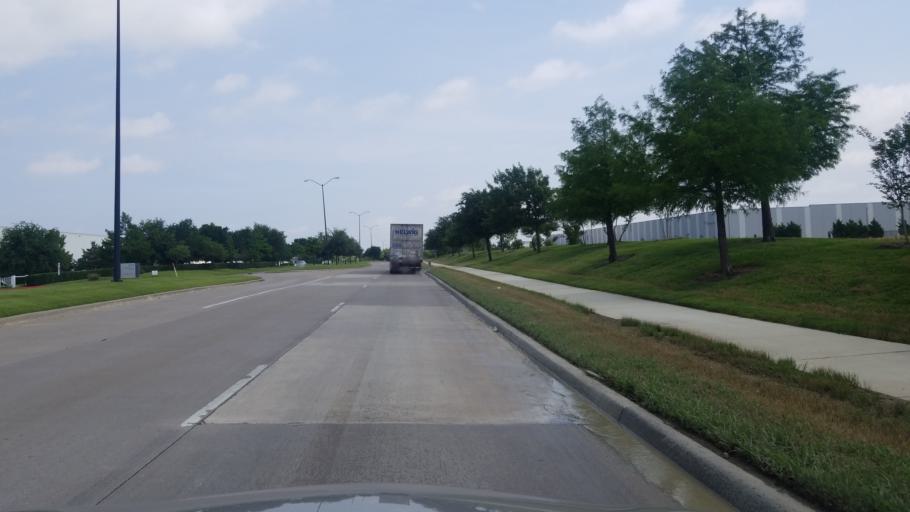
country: US
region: Texas
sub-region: Dallas County
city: Duncanville
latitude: 32.6814
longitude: -96.9651
